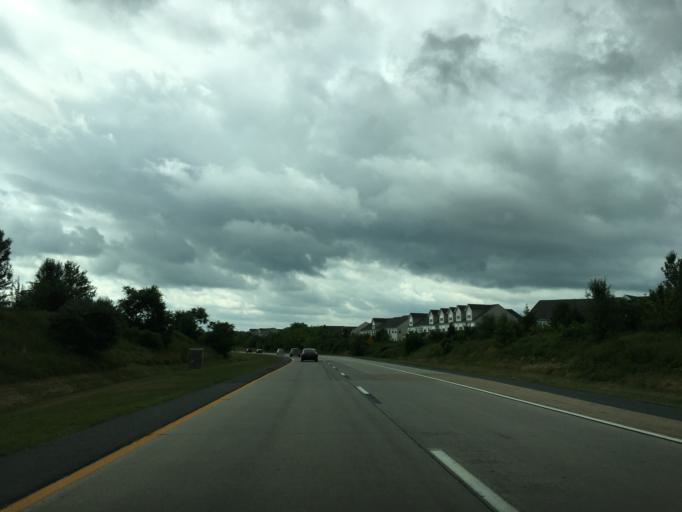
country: US
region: Delaware
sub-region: New Castle County
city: Middletown
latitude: 39.4533
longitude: -75.6762
